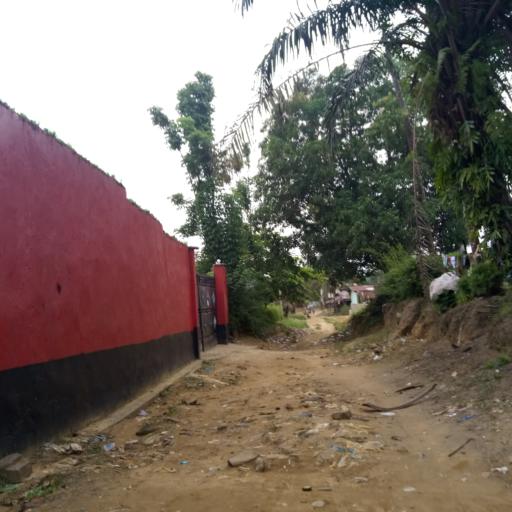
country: LR
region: Montserrado
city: Monrovia
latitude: 6.2978
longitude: -10.6861
